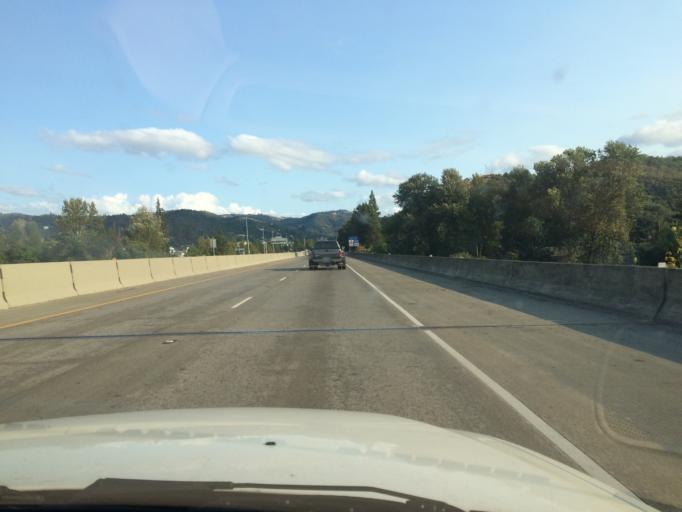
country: US
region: Oregon
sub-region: Douglas County
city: Roseburg
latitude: 43.2200
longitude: -123.3585
